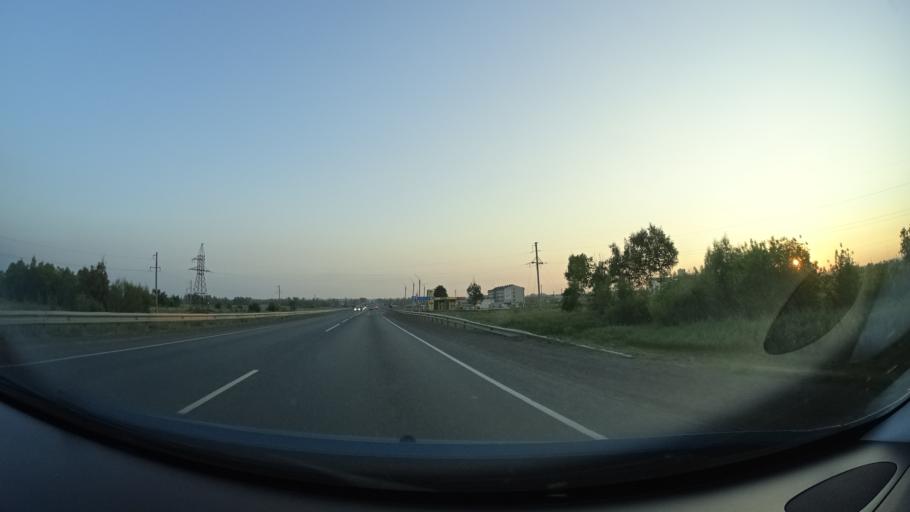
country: RU
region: Samara
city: Sernovodsk
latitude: 53.8900
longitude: 51.2574
